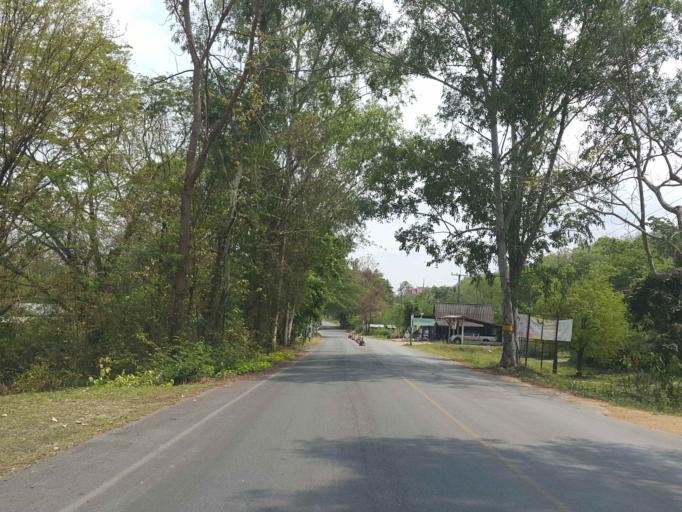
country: TH
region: Lampang
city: Thoen
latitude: 17.5977
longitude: 99.3320
